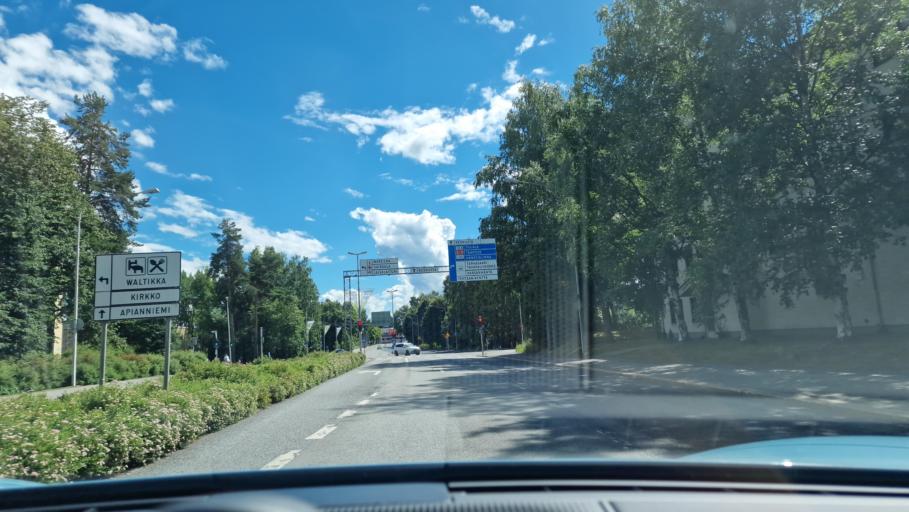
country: FI
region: Pirkanmaa
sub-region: Etelae-Pirkanmaa
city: Valkeakoski
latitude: 61.2717
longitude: 24.0212
